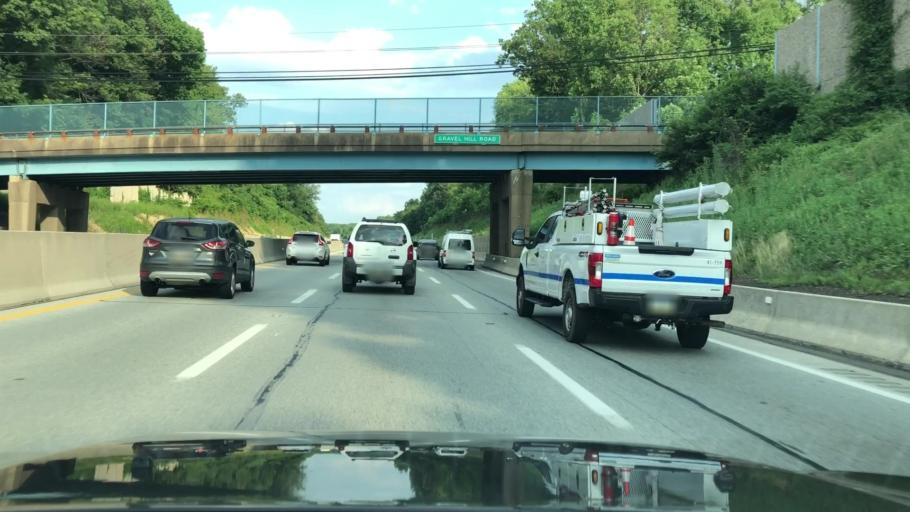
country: US
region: Pennsylvania
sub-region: Bucks County
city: Feasterville
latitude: 40.1562
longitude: -75.0355
